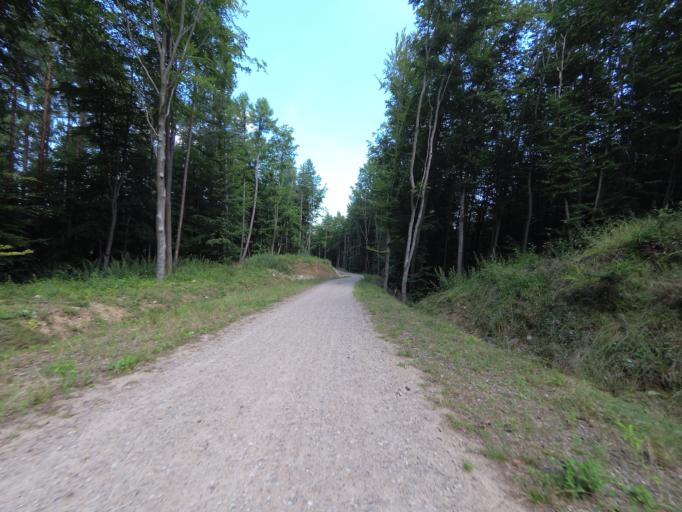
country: PL
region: Pomeranian Voivodeship
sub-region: Gdynia
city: Wielki Kack
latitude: 54.4824
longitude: 18.5020
